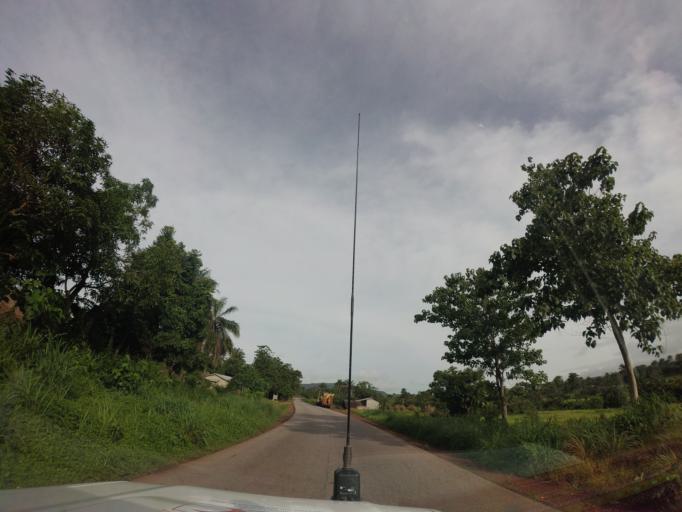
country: GN
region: Kindia
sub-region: Kindia
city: Kindia
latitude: 9.9011
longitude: -13.0263
